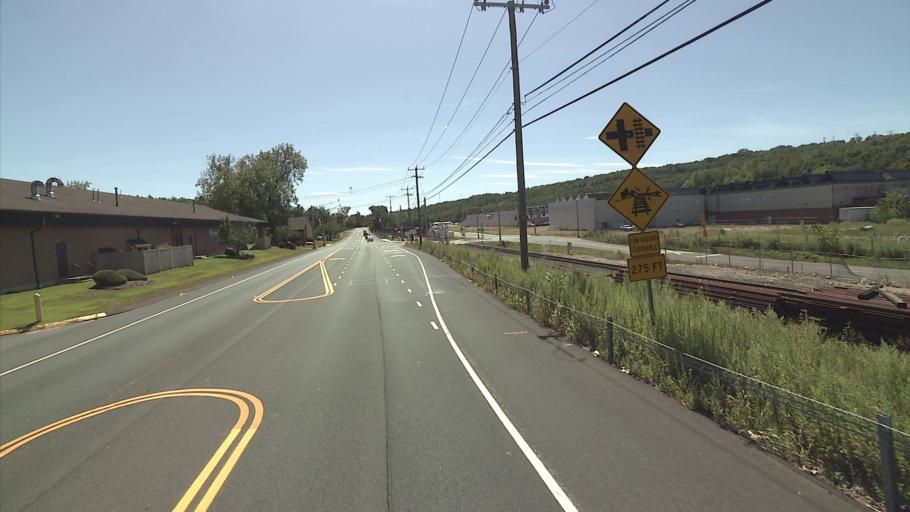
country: US
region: Connecticut
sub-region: Litchfield County
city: Oakville
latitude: 41.5994
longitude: -73.0580
